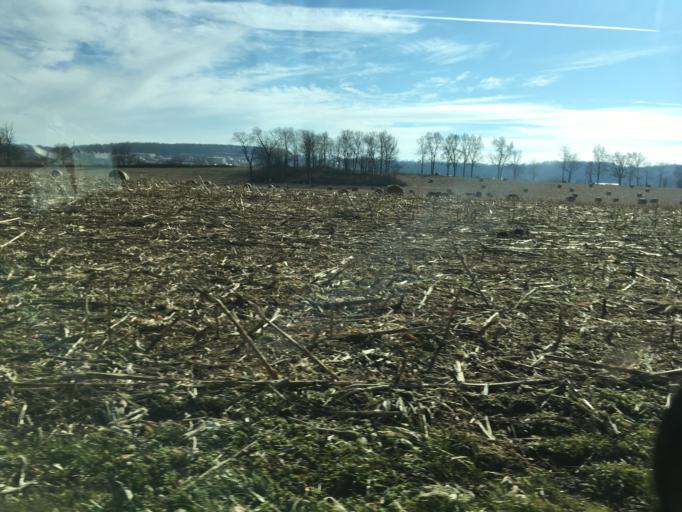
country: US
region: Pennsylvania
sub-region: Berks County
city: Kutztown
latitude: 40.4864
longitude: -75.7741
